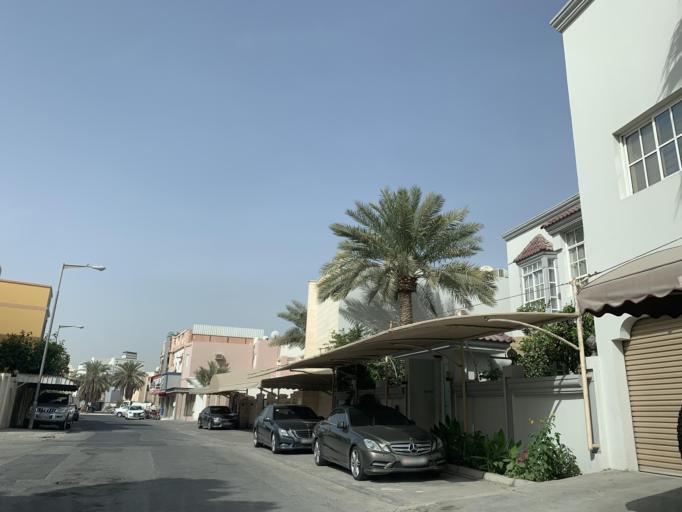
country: BH
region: Northern
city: Madinat `Isa
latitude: 26.1749
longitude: 50.5615
